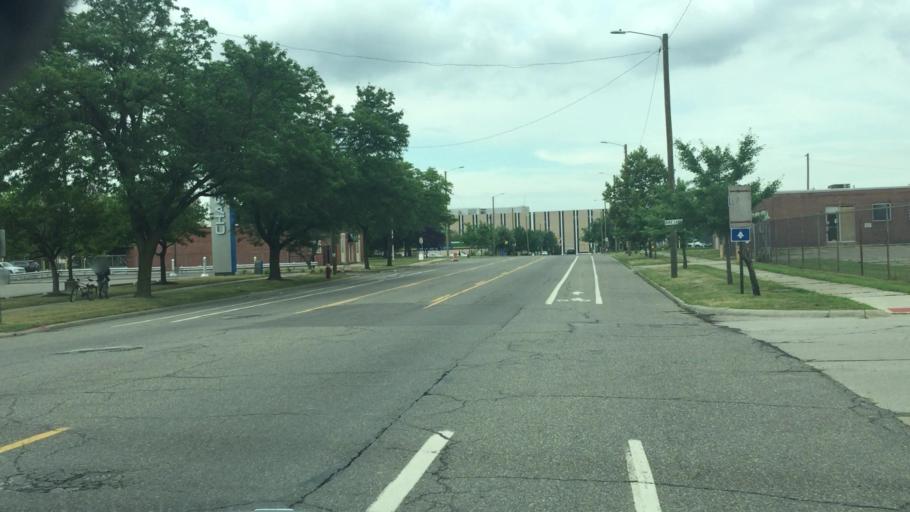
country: US
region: Michigan
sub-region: Wayne County
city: Detroit
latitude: 42.3288
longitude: -83.0650
